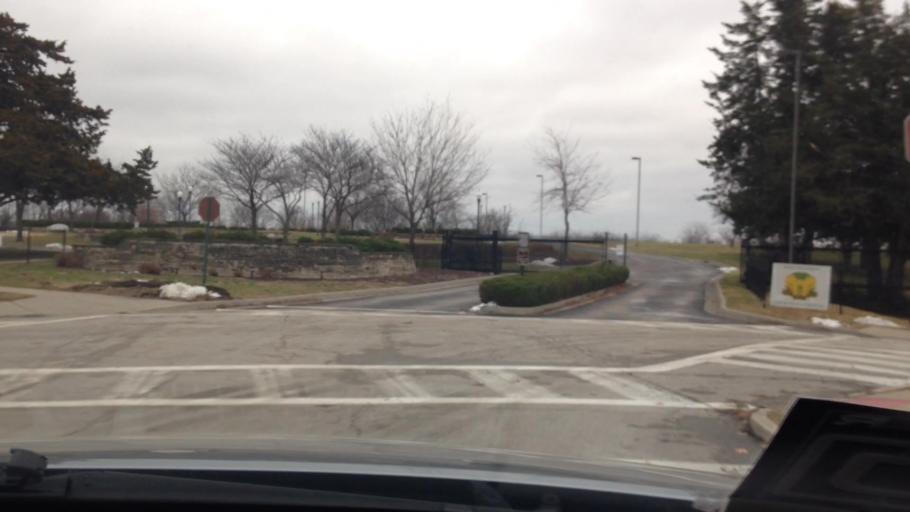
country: US
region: Kansas
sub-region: Leavenworth County
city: Leavenworth
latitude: 39.3397
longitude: -94.9182
